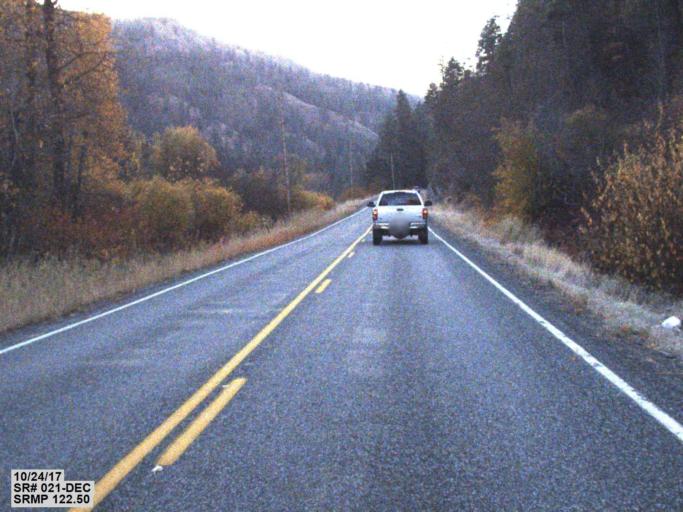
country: US
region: Washington
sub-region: Okanogan County
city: Coulee Dam
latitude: 48.1560
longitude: -118.7011
